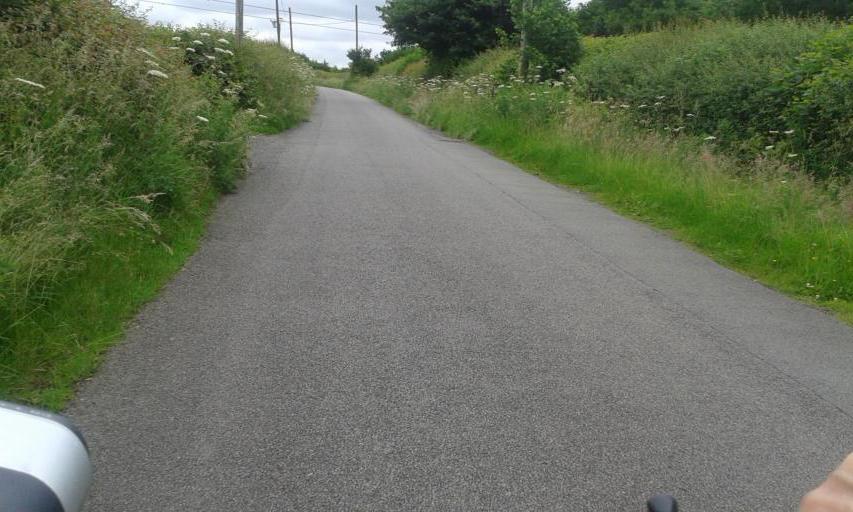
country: GB
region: England
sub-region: Leicestershire
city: Earl Shilton
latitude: 52.5794
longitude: -1.2905
